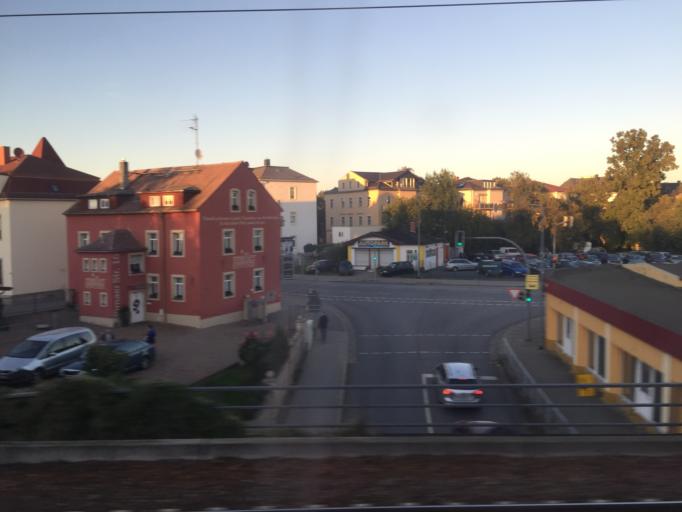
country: DE
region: Saxony
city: Heidenau
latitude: 50.9734
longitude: 13.8720
